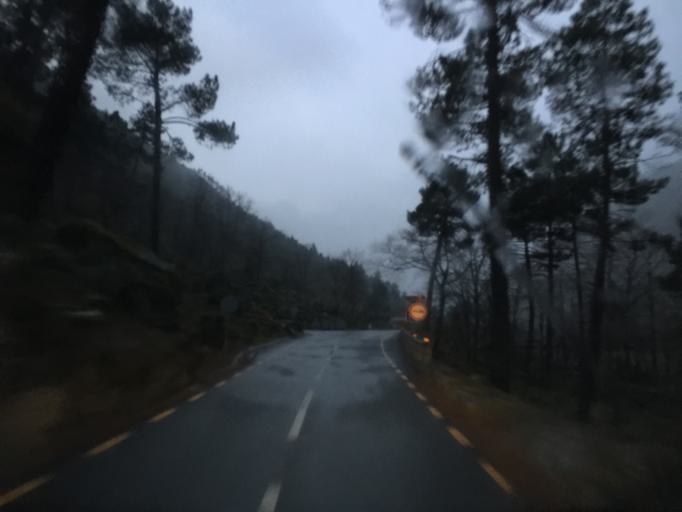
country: PT
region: Guarda
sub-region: Manteigas
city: Manteigas
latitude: 40.3695
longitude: -7.5505
